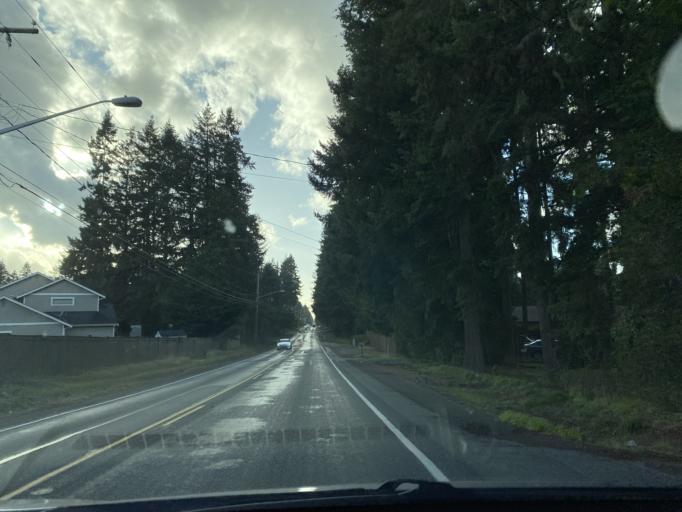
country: US
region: Washington
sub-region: Pierce County
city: South Hill
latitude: 47.1184
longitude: -122.2840
